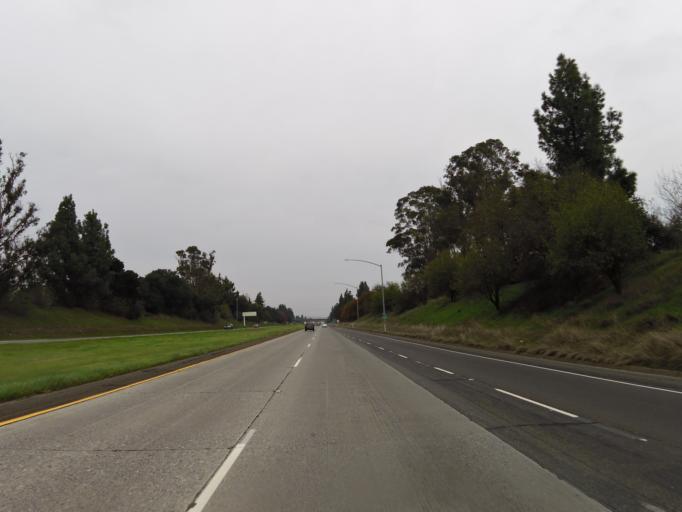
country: US
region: California
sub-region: Yolo County
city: Davis
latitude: 38.5498
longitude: -121.7678
